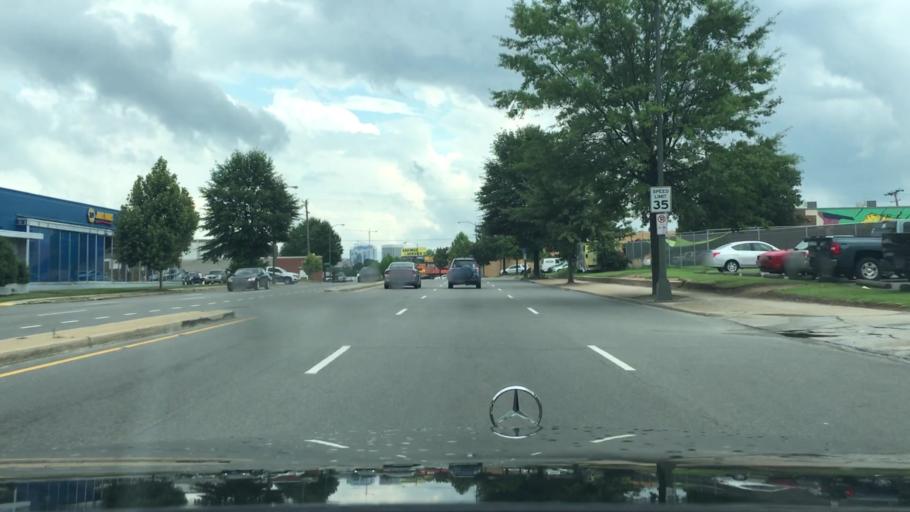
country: US
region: Virginia
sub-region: City of Richmond
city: Richmond
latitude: 37.5587
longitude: -77.4426
